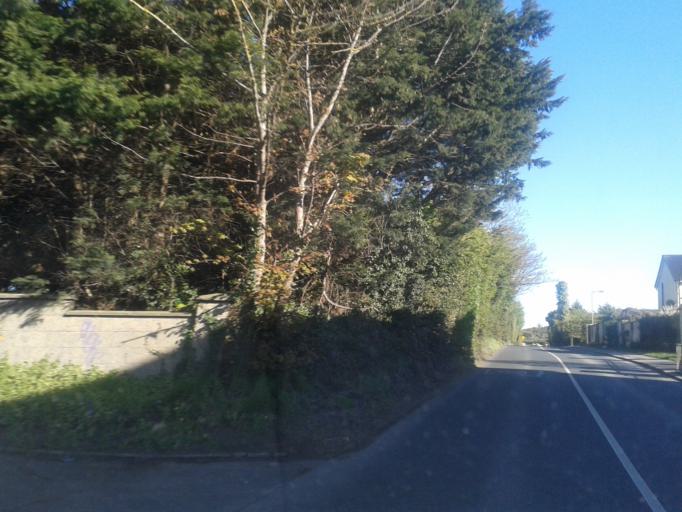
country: IE
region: Leinster
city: Kinsealy-Drinan
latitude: 53.4437
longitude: -6.1956
